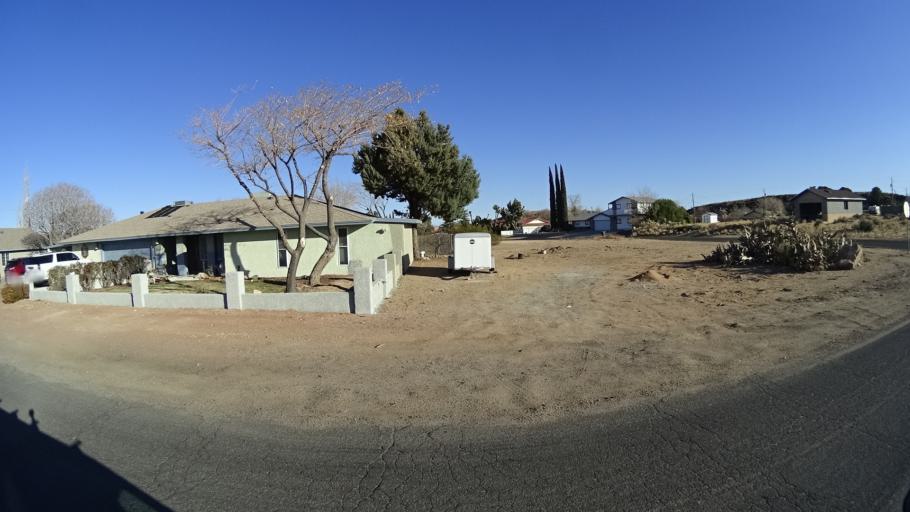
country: US
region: Arizona
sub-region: Mohave County
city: Kingman
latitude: 35.2031
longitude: -114.0100
